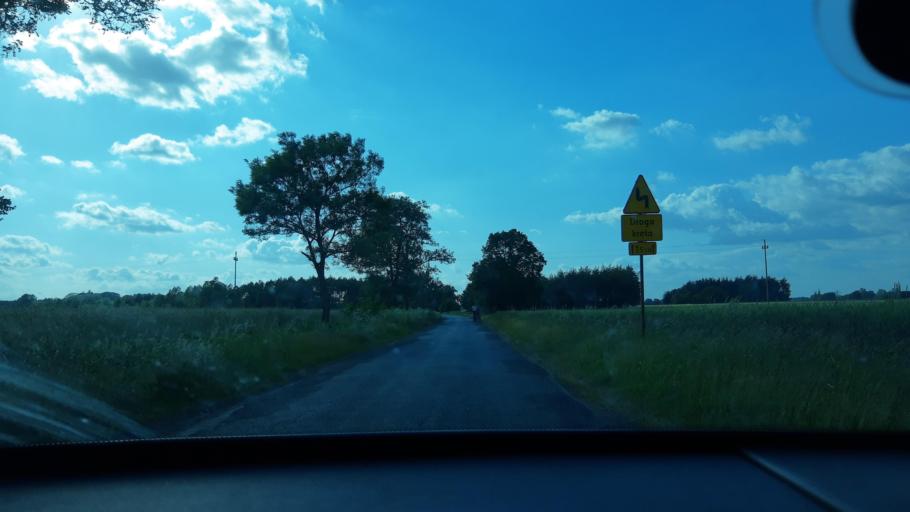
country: PL
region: Lodz Voivodeship
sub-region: Powiat zdunskowolski
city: Zapolice
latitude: 51.5380
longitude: 18.8267
